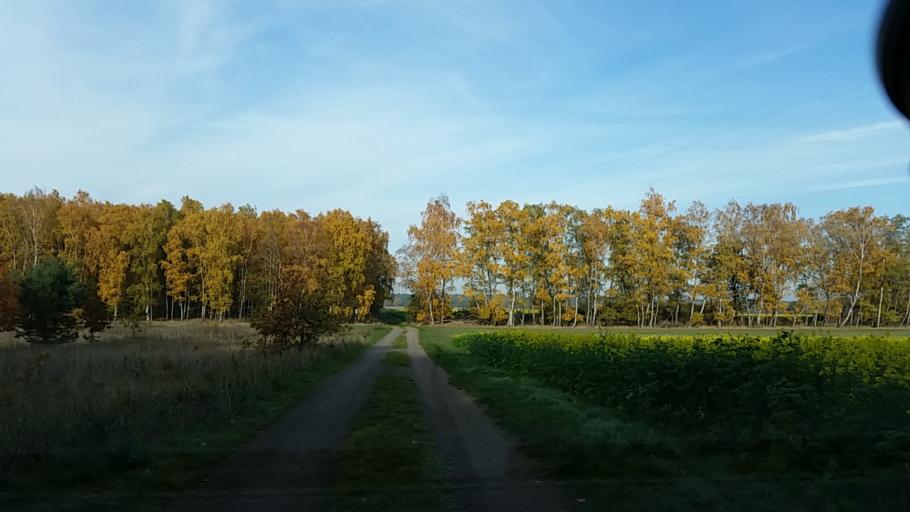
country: DE
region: Lower Saxony
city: Weyhausen
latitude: 52.4763
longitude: 10.7185
